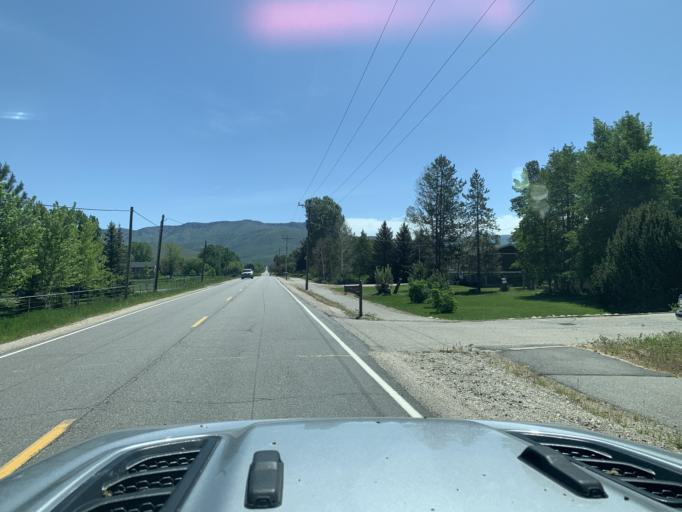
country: US
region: Utah
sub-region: Weber County
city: Wolf Creek
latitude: 41.2933
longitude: -111.8026
